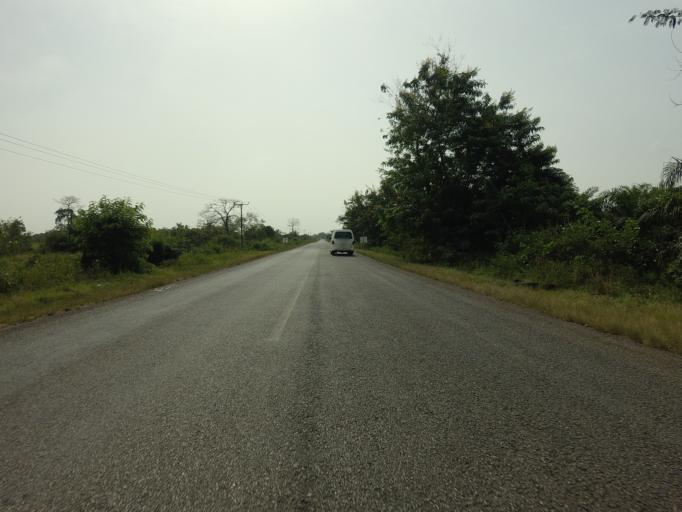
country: GH
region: Volta
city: Ho
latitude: 6.3951
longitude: 0.1803
